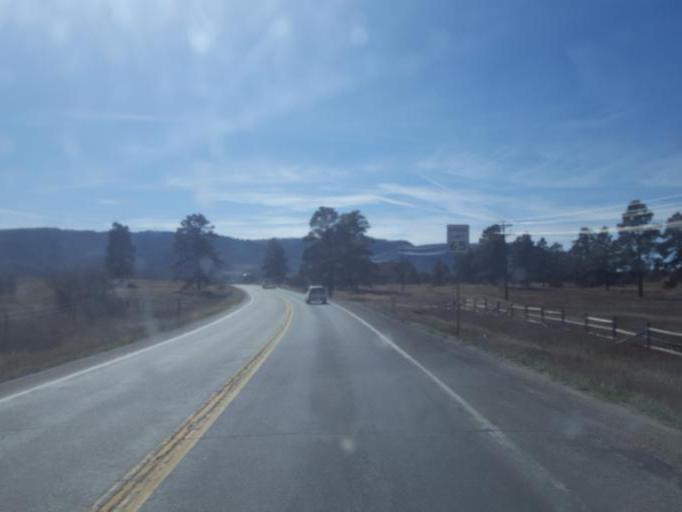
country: US
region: Colorado
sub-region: Archuleta County
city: Pagosa Springs
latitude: 37.2419
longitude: -107.0990
